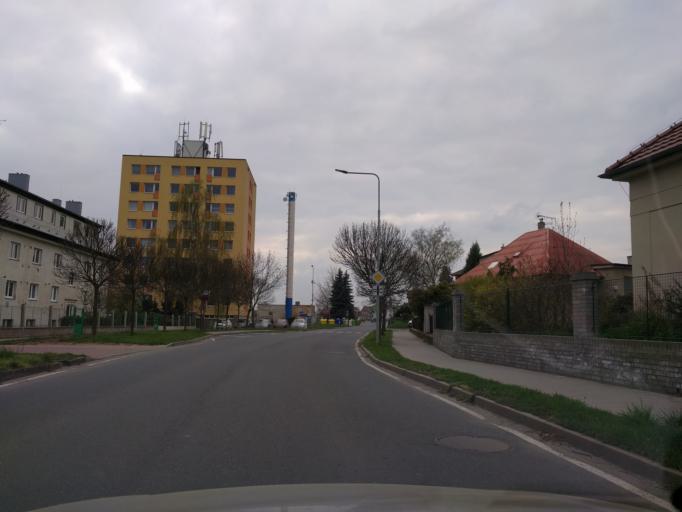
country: CZ
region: Central Bohemia
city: Cesky Brod
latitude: 50.0695
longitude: 14.8522
